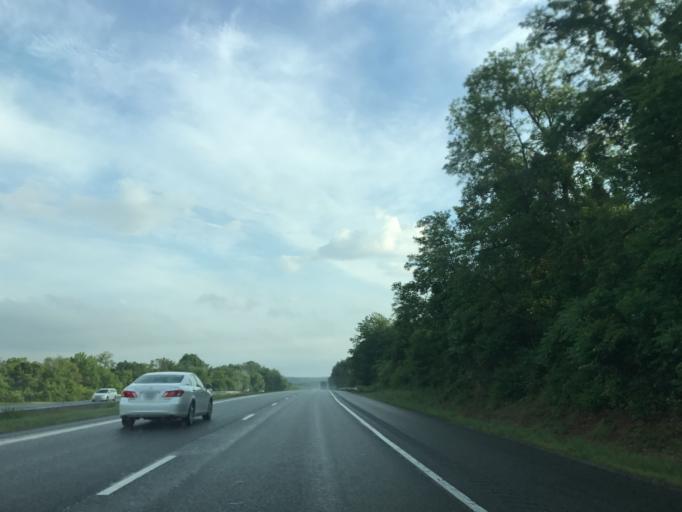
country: US
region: Pennsylvania
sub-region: York County
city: New Freedom
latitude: 39.6739
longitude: -76.6454
